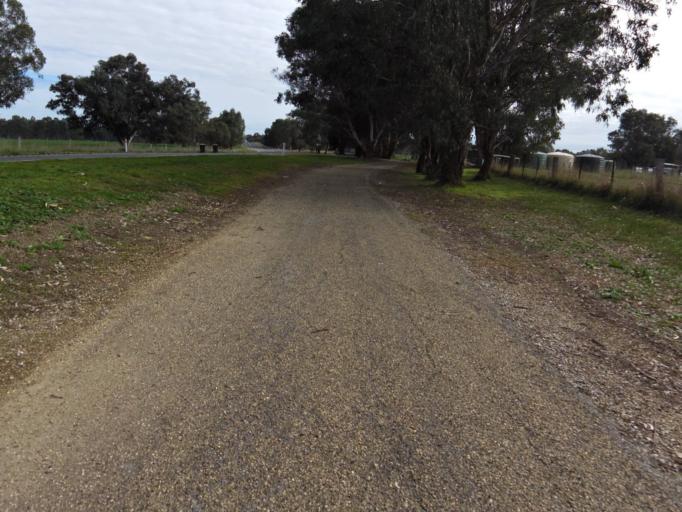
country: AU
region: Victoria
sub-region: Wangaratta
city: Wangaratta
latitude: -36.3971
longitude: 146.3447
